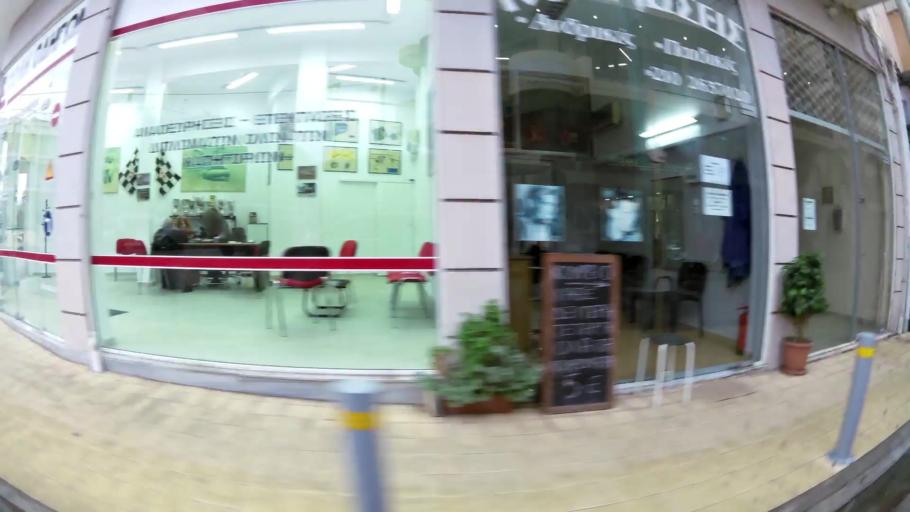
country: GR
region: Attica
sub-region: Nomarchia Athinas
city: Agioi Anargyroi
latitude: 38.0313
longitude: 23.7238
